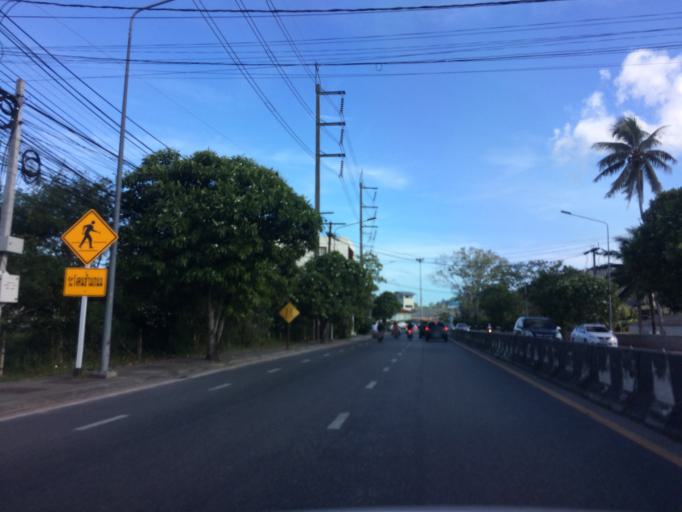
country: TH
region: Phuket
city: Kathu
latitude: 7.9058
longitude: 98.3510
